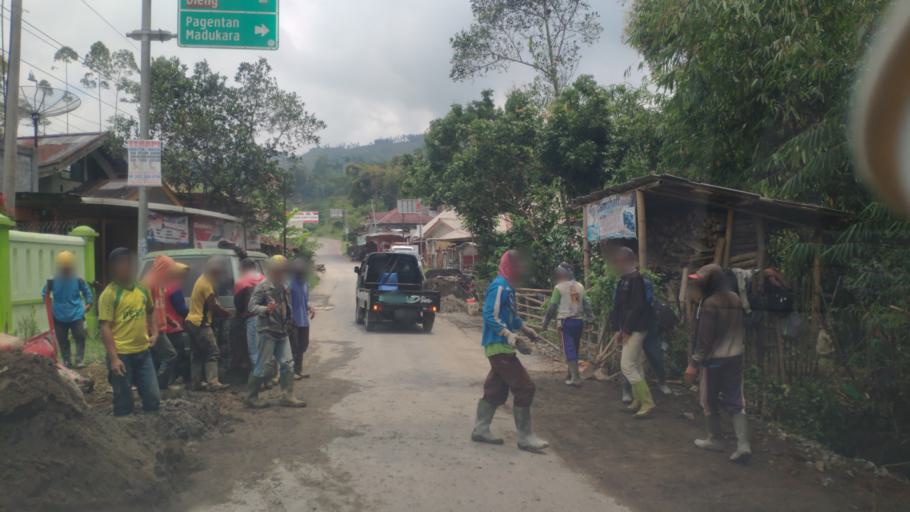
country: ID
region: Central Java
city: Wonosobo
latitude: -7.2464
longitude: 109.8011
